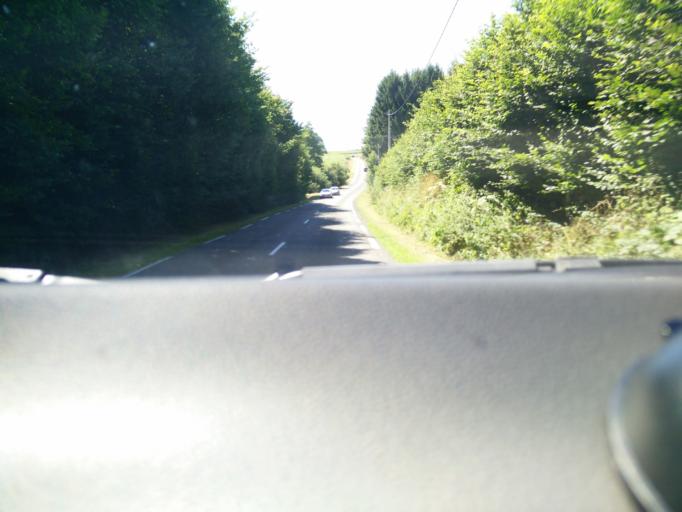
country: FR
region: Nord-Pas-de-Calais
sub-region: Departement du Nord
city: Sains-du-Nord
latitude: 50.1534
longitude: 4.0820
